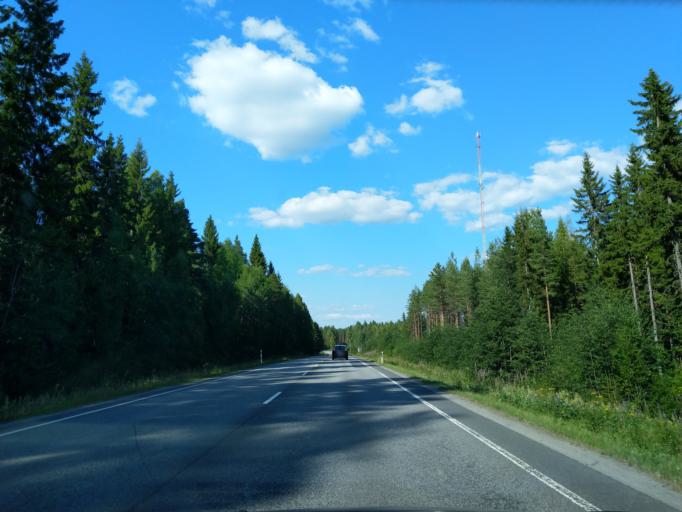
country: FI
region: Pirkanmaa
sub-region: Luoteis-Pirkanmaa
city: Kihnioe
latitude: 62.1500
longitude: 23.1574
